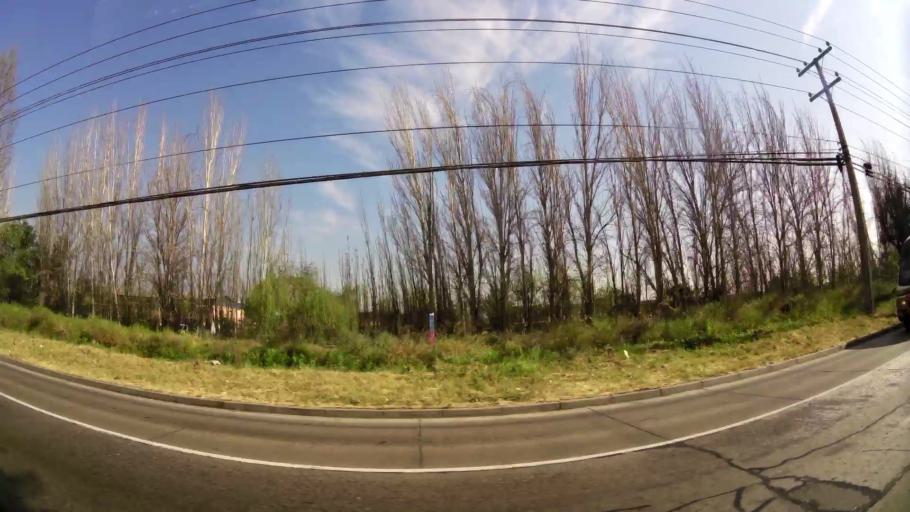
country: CL
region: Santiago Metropolitan
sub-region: Provincia de Maipo
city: San Bernardo
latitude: -33.5402
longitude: -70.7759
